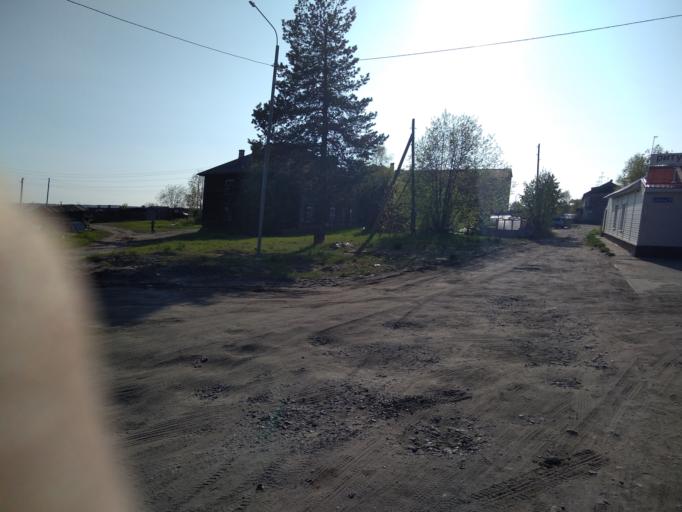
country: RU
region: Komi Republic
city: Puteyets
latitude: 65.1094
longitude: 57.1412
